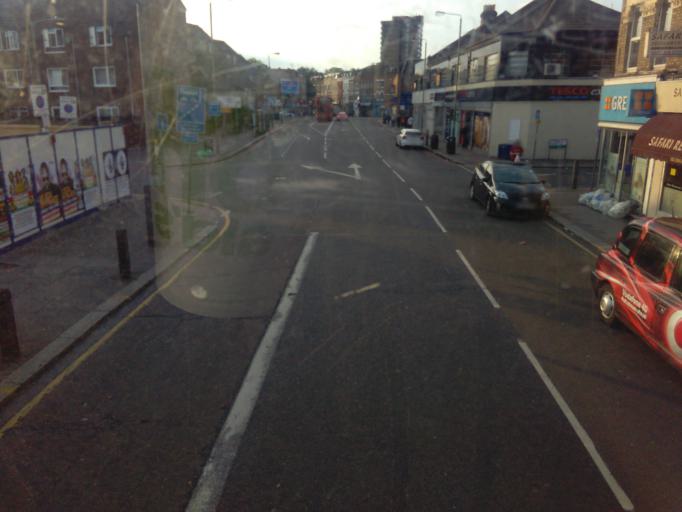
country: GB
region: England
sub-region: Greater London
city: Battersea
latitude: 51.4690
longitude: -0.1711
